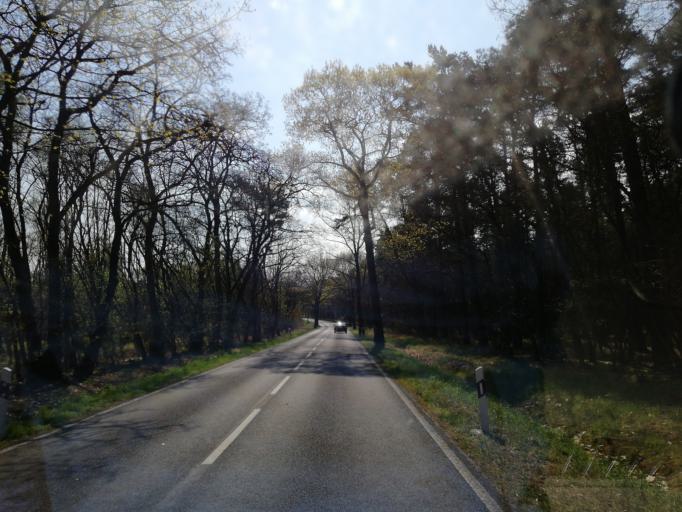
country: DE
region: Brandenburg
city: Calau
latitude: 51.7752
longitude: 13.8933
